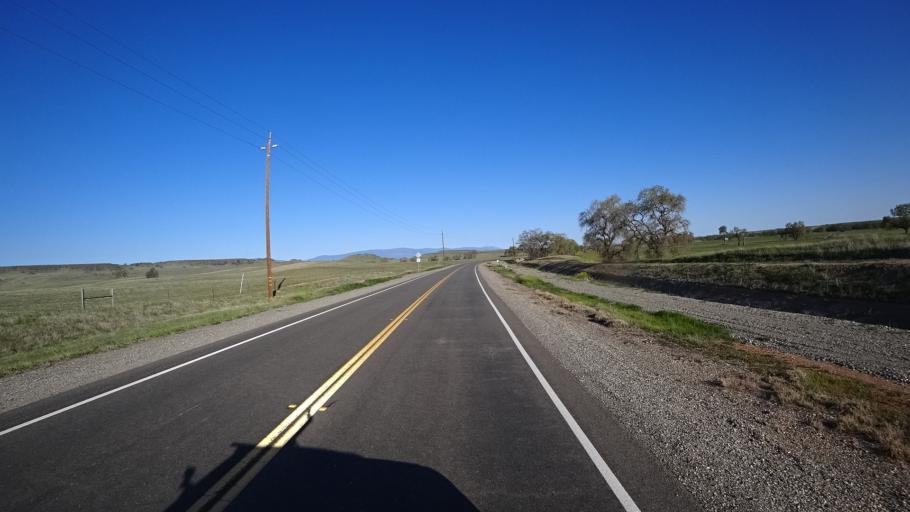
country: US
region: California
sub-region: Glenn County
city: Orland
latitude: 39.7889
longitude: -122.3082
